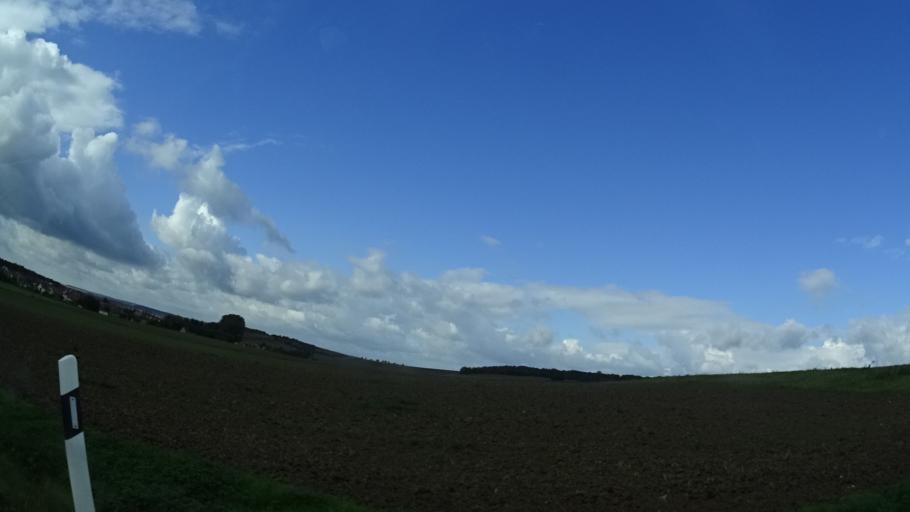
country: DE
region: Bavaria
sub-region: Regierungsbezirk Unterfranken
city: Frankenwinheim
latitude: 49.8620
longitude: 10.3032
